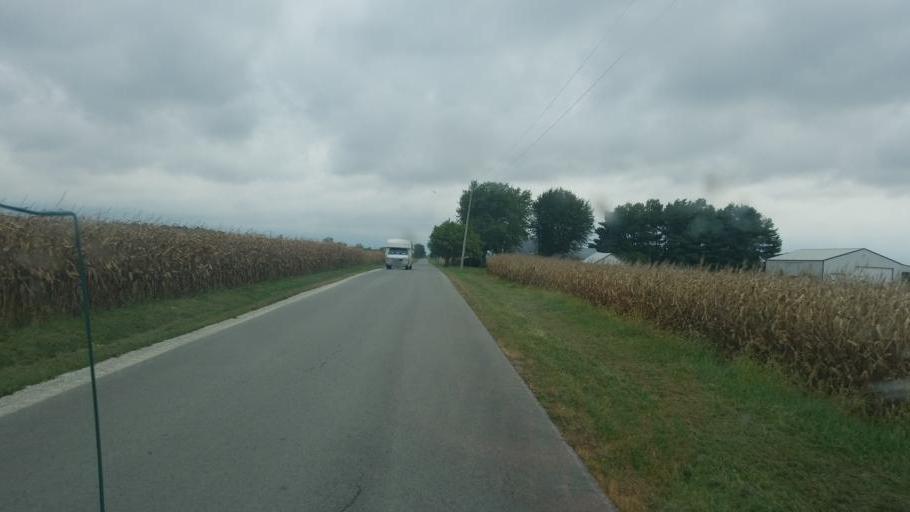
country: US
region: Ohio
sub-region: Seneca County
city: Fostoria
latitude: 41.0914
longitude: -83.5165
